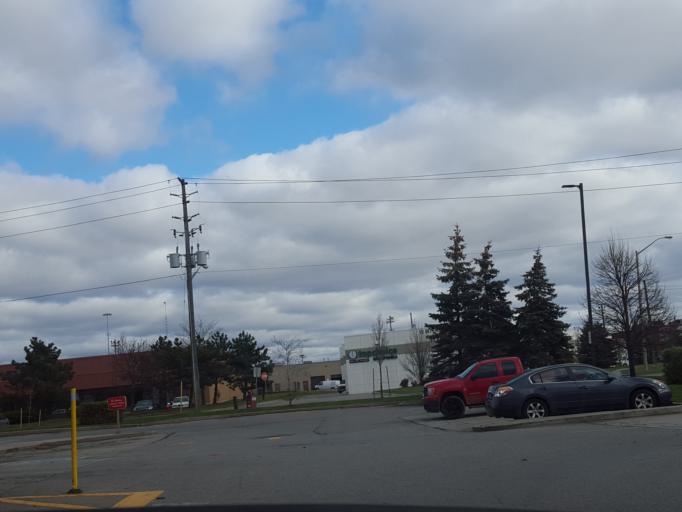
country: CA
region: Ontario
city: Brampton
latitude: 43.7313
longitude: -79.6782
